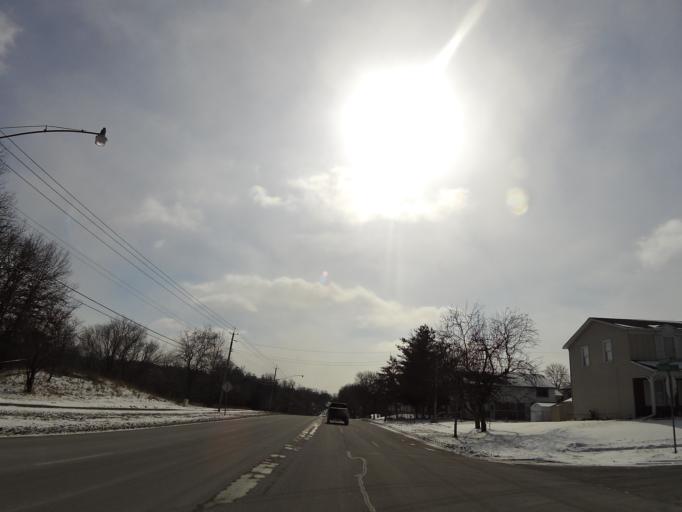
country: US
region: Minnesota
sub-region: Ramsey County
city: Maplewood
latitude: 44.9371
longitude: -93.0049
